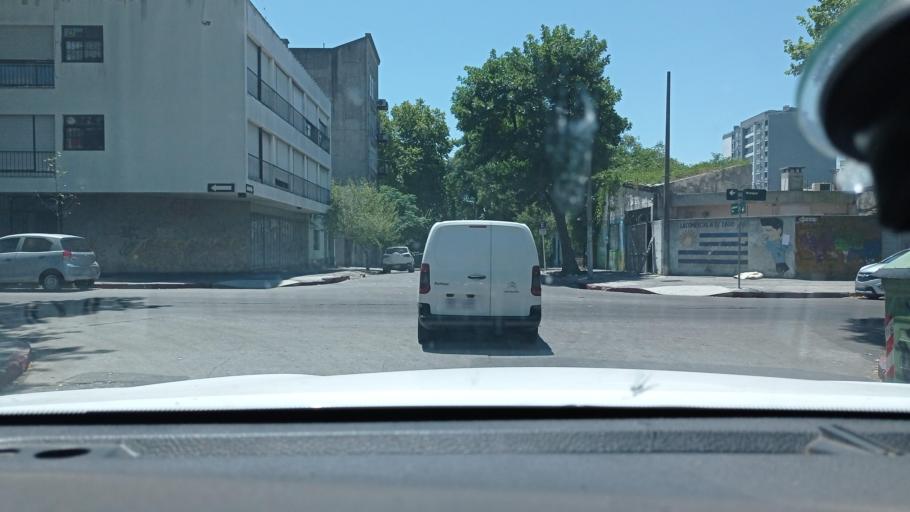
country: UY
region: Montevideo
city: Montevideo
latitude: -34.8910
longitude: -56.1666
